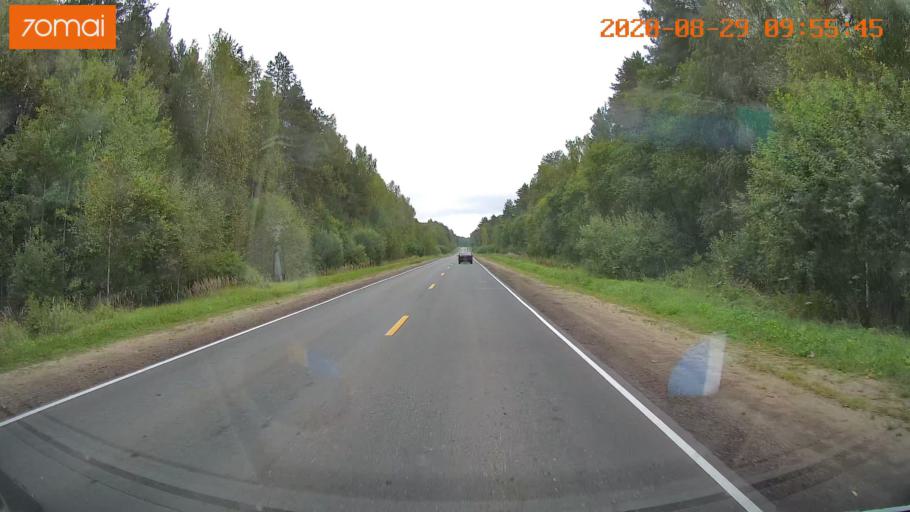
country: RU
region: Ivanovo
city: Zarechnyy
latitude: 57.4218
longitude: 42.2716
